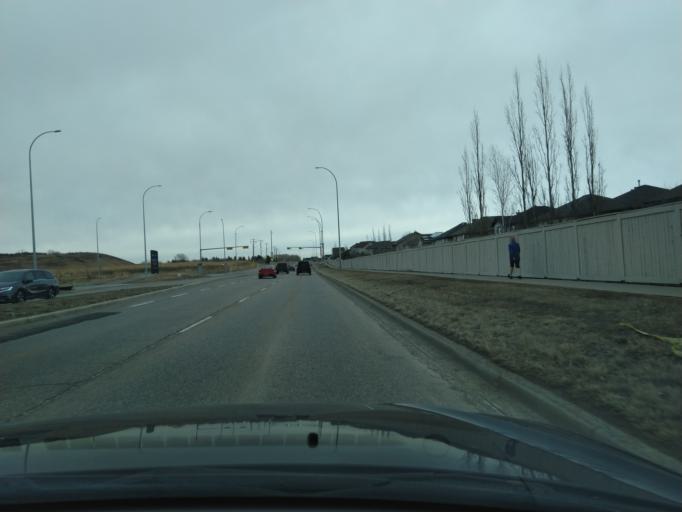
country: CA
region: Alberta
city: Calgary
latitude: 51.1540
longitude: -114.2310
